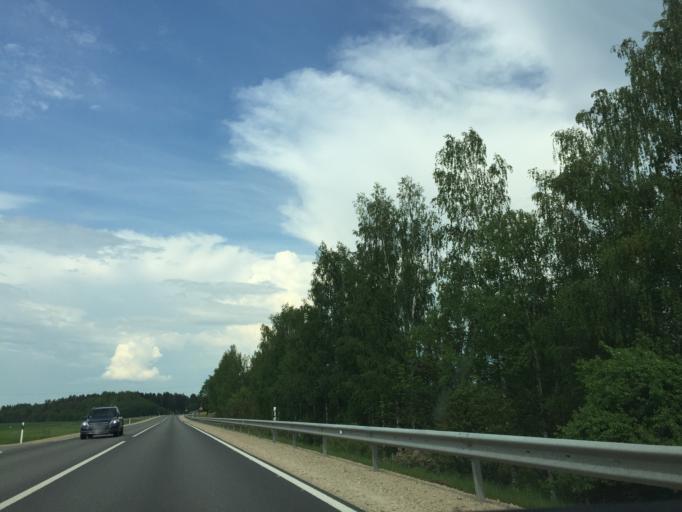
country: LV
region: Varaklani
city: Varaklani
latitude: 56.5957
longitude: 26.7252
